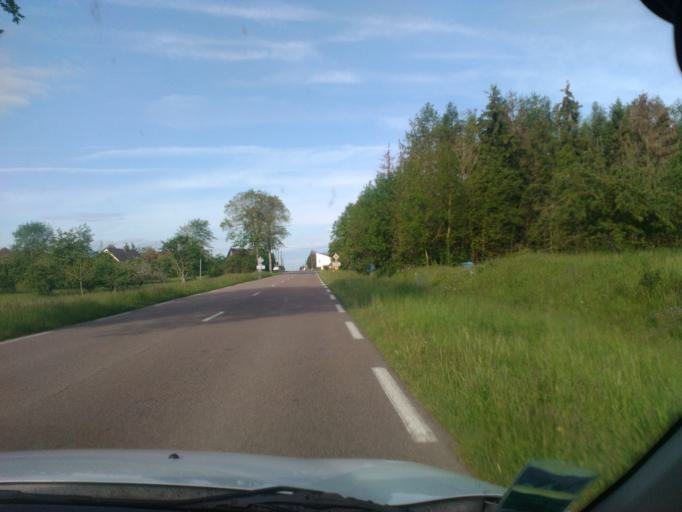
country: FR
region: Champagne-Ardenne
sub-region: Departement de l'Aube
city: Vendeuvre-sur-Barse
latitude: 48.2443
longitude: 4.5431
